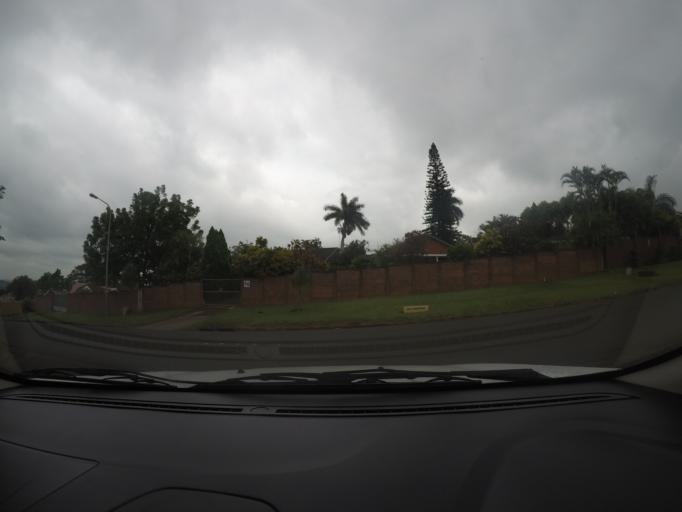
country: ZA
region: KwaZulu-Natal
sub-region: uThungulu District Municipality
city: Empangeni
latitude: -28.7683
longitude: 31.8920
